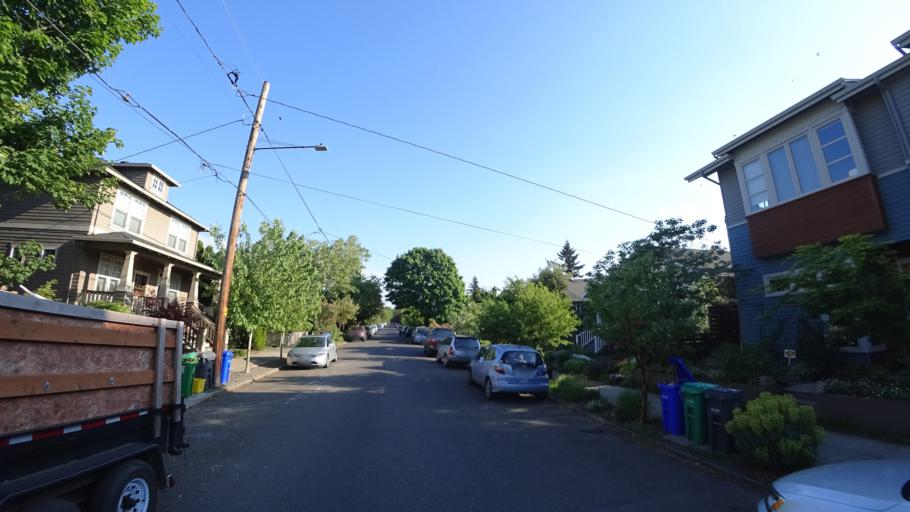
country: US
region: Oregon
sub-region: Multnomah County
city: Portland
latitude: 45.5586
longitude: -122.6389
